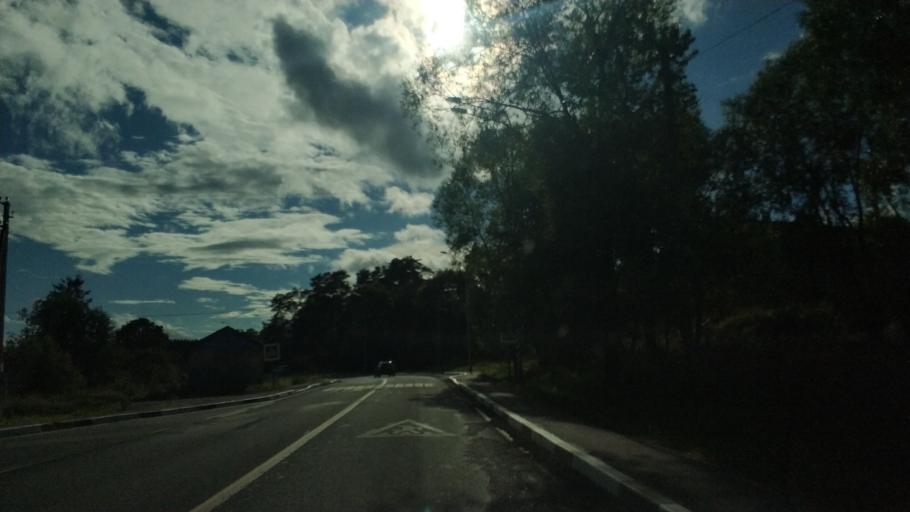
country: RU
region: Republic of Karelia
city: Lakhdenpokh'ya
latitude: 61.5519
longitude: 30.3190
